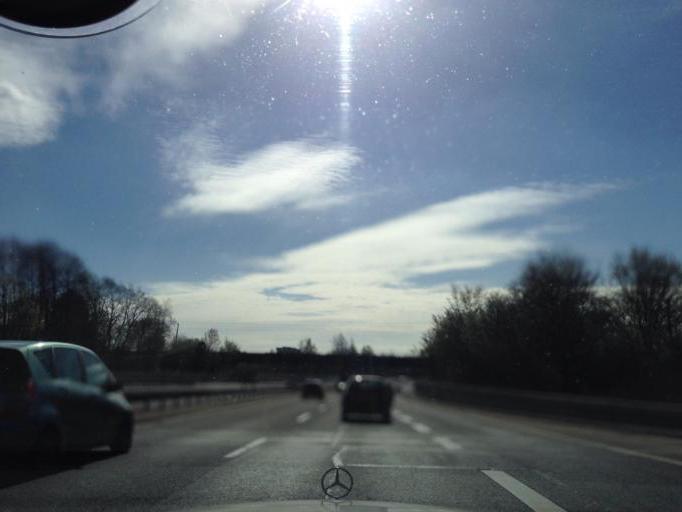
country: DE
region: Lower Saxony
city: Laatzen
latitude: 52.3551
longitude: 9.7882
